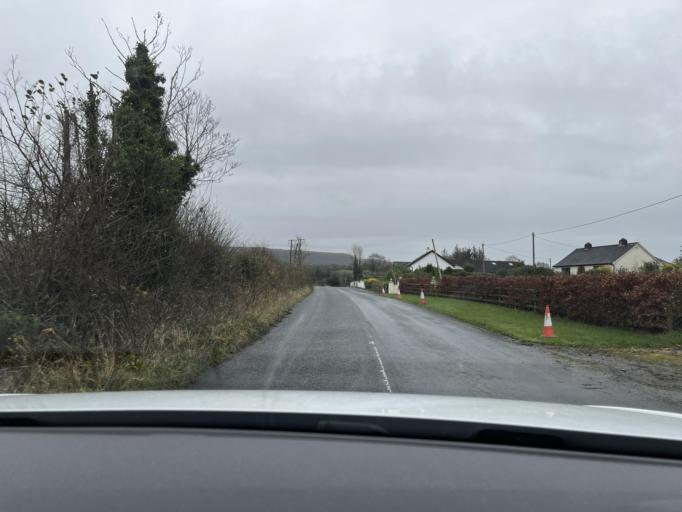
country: IE
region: Connaught
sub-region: County Leitrim
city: Manorhamilton
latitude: 54.2974
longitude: -8.1994
